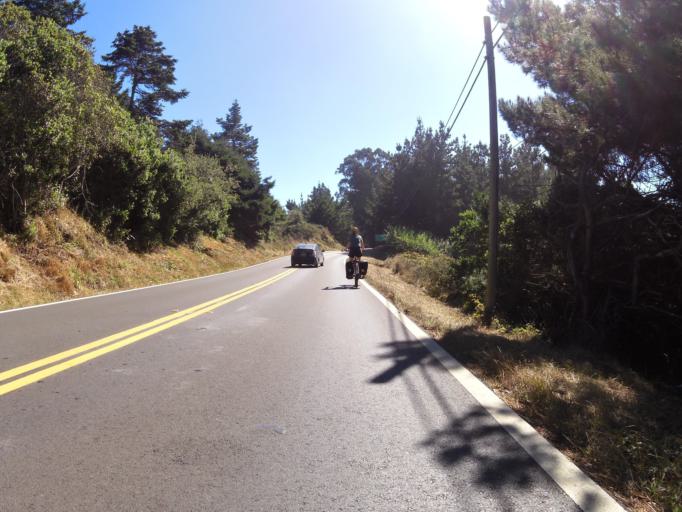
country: US
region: California
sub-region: Mendocino County
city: Fort Bragg
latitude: 39.6295
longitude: -123.7824
